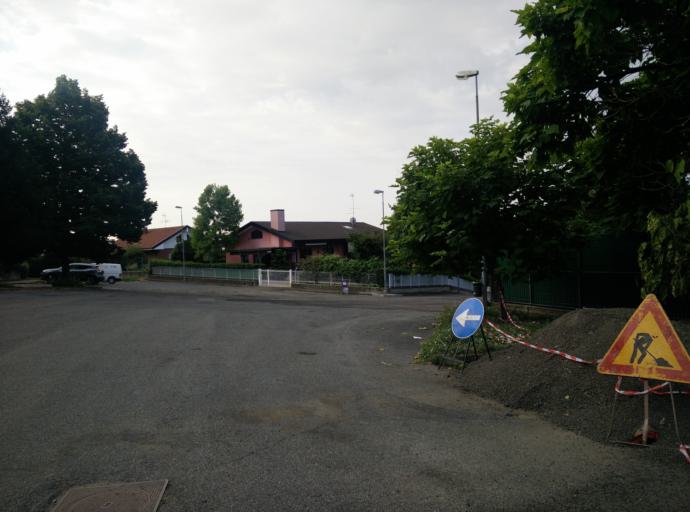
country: IT
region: Piedmont
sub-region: Provincia di Torino
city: Revigliasco
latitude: 44.9949
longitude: 7.7246
